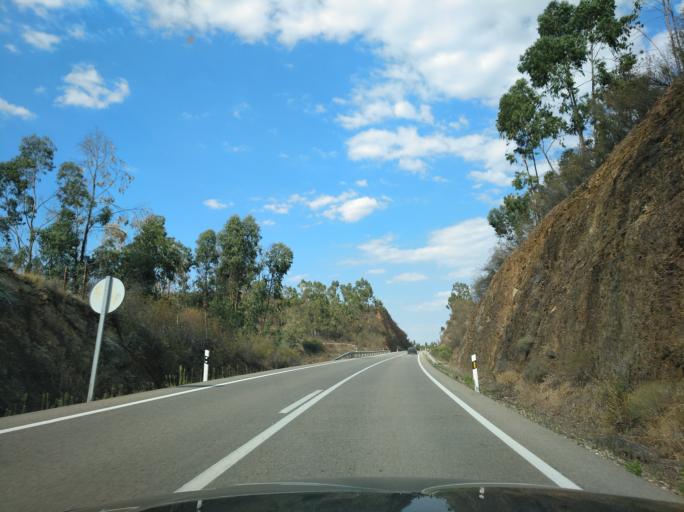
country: ES
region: Andalusia
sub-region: Provincia de Huelva
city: Santa Barbara de Casa
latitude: 37.8791
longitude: -7.2126
